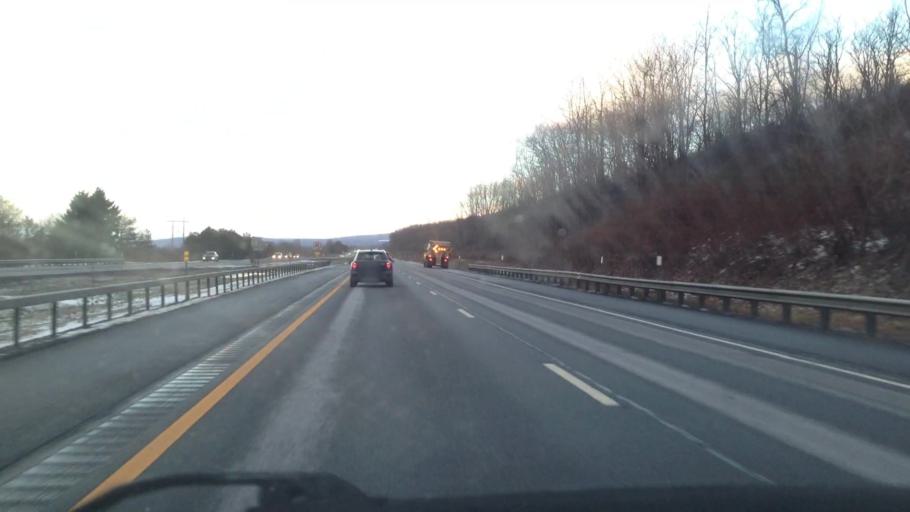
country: US
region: New York
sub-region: Herkimer County
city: Frankfort
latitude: 43.0362
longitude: -75.0487
